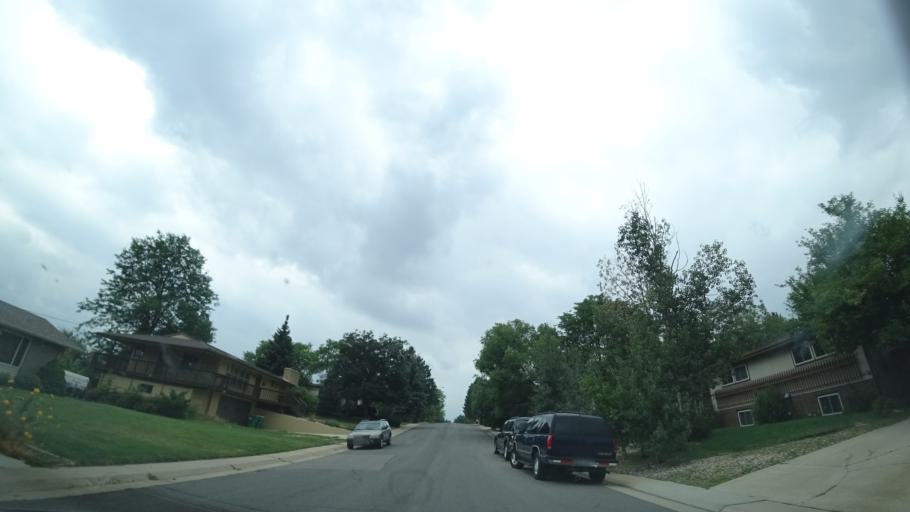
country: US
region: Colorado
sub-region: Jefferson County
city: West Pleasant View
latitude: 39.7003
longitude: -105.1487
